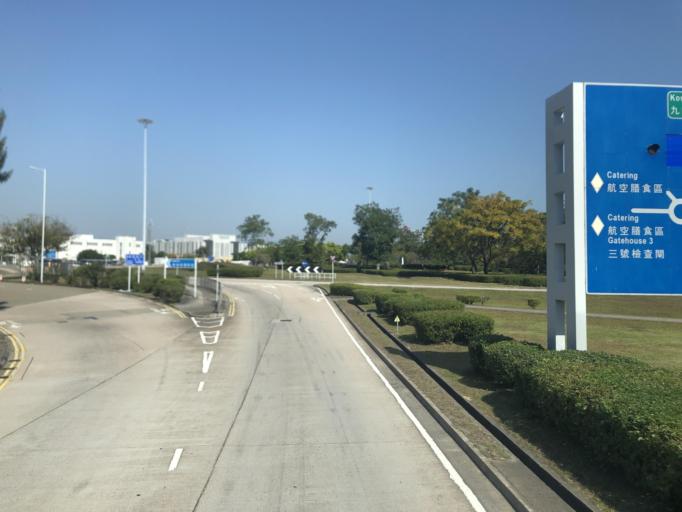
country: HK
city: Tai O
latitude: 22.2983
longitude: 113.9318
